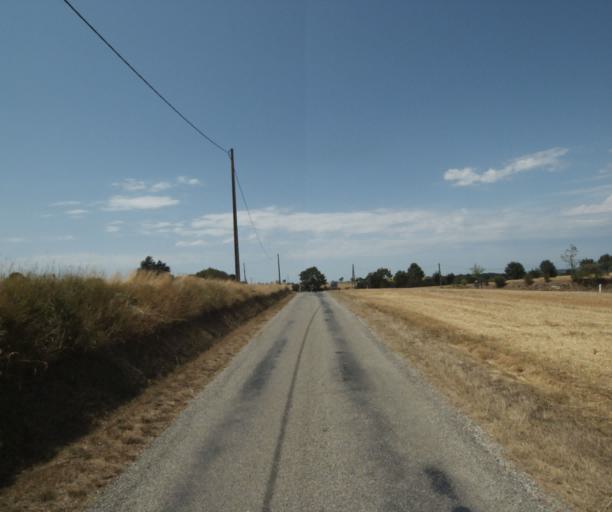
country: FR
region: Midi-Pyrenees
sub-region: Departement de la Haute-Garonne
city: Saint-Felix-Lauragais
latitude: 43.4592
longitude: 1.8503
